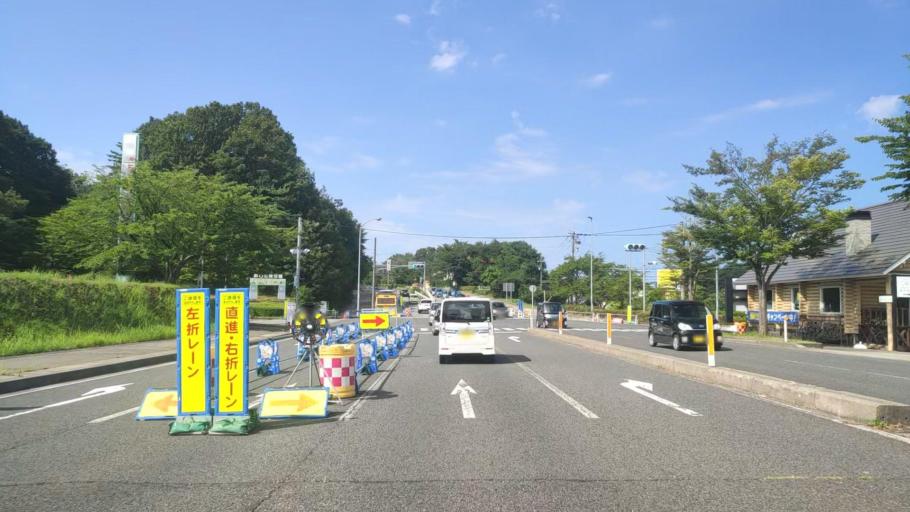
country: JP
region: Ishikawa
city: Matsuto
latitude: 36.4411
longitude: 136.5458
